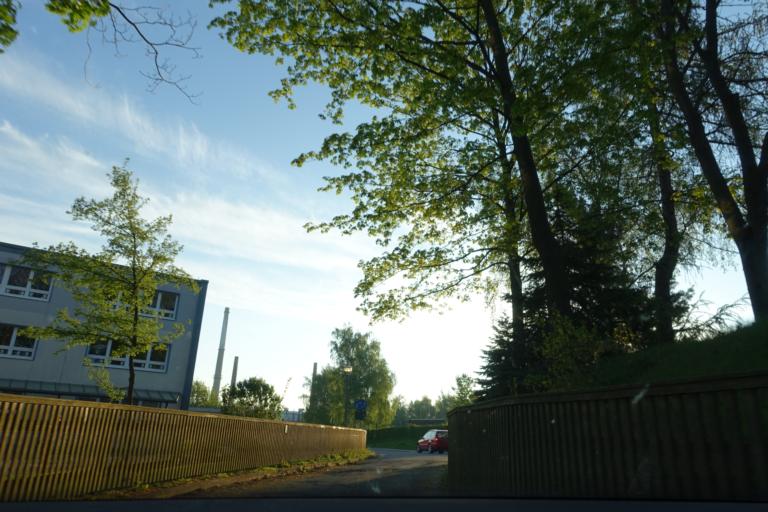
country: DE
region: Saxony
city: Brand-Erbisdorf
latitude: 50.8674
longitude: 13.3285
